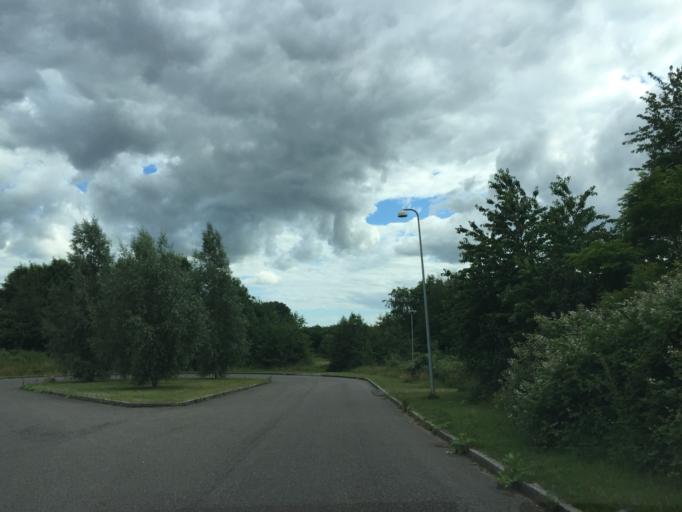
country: DK
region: South Denmark
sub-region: Odense Kommune
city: Hojby
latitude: 55.3487
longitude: 10.3937
